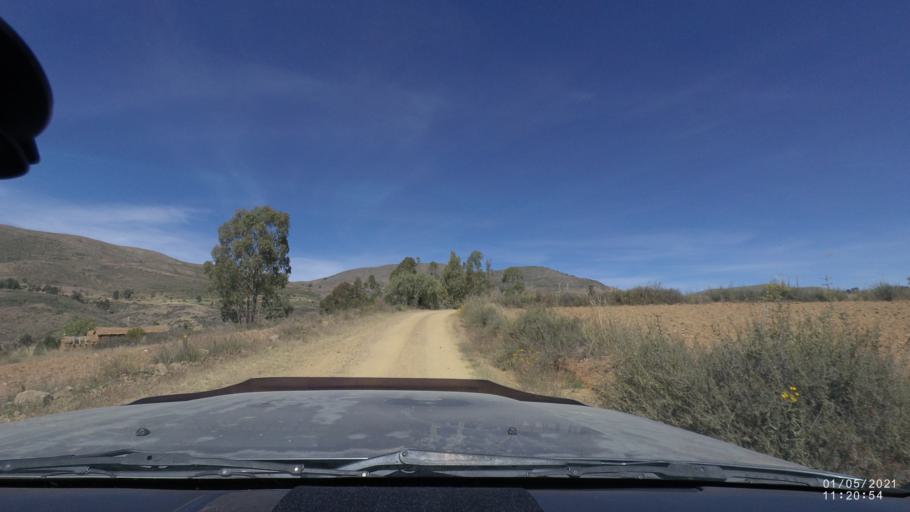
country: BO
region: Cochabamba
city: Tarata
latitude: -17.6437
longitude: -66.1249
